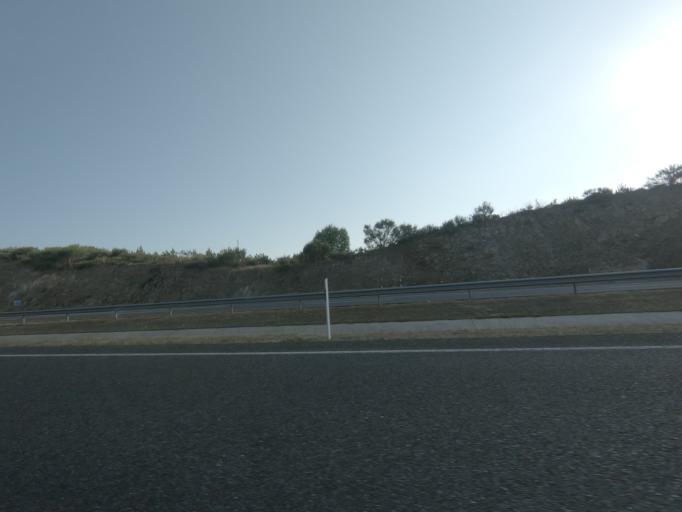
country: ES
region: Galicia
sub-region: Provincia de Ourense
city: Oimbra
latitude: 41.8593
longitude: -7.4251
